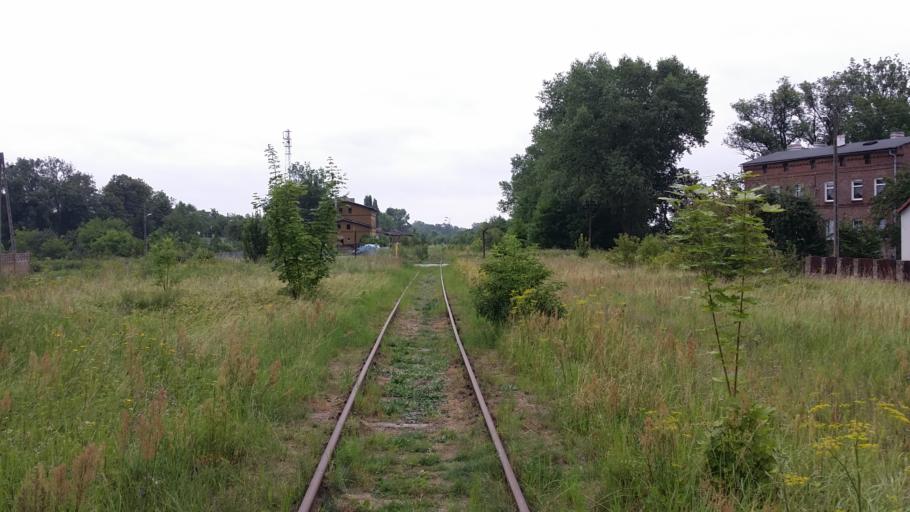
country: PL
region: West Pomeranian Voivodeship
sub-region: Powiat choszczenski
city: Drawno
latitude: 53.2137
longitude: 15.7688
